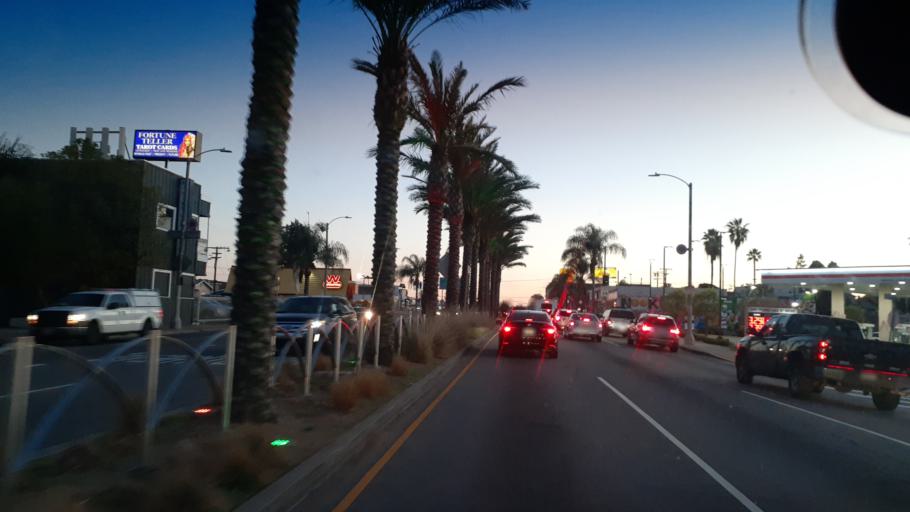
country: US
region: California
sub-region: Los Angeles County
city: San Pedro
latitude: 33.7459
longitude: -118.2924
